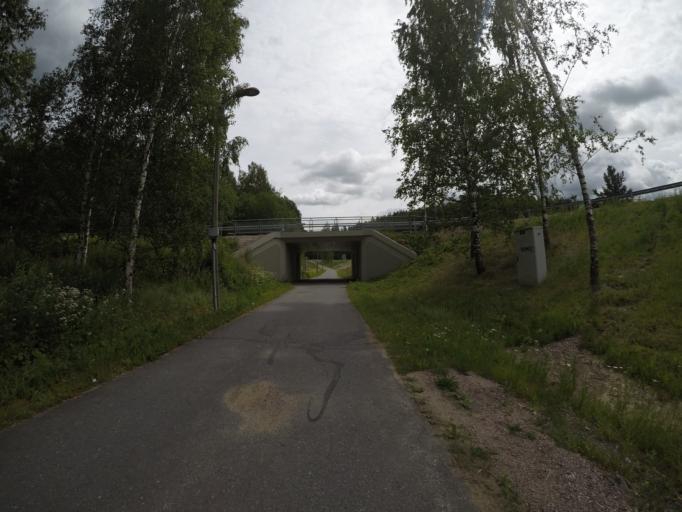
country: FI
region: Haeme
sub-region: Haemeenlinna
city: Haemeenlinna
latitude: 60.9844
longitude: 24.5074
